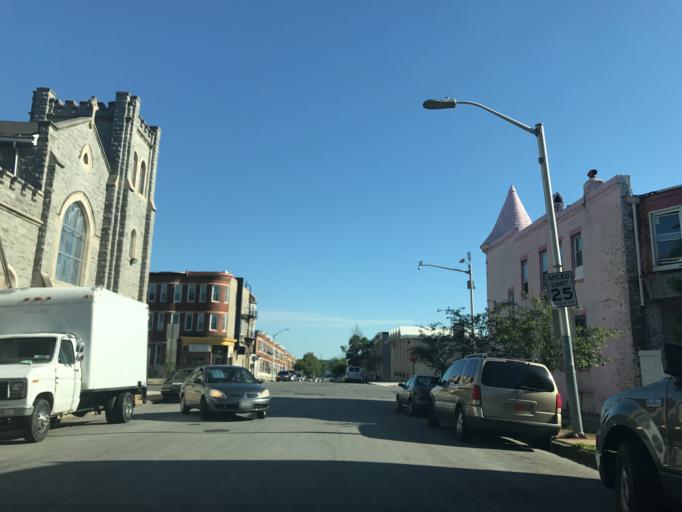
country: US
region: Maryland
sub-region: City of Baltimore
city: Baltimore
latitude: 39.3103
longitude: -76.6500
